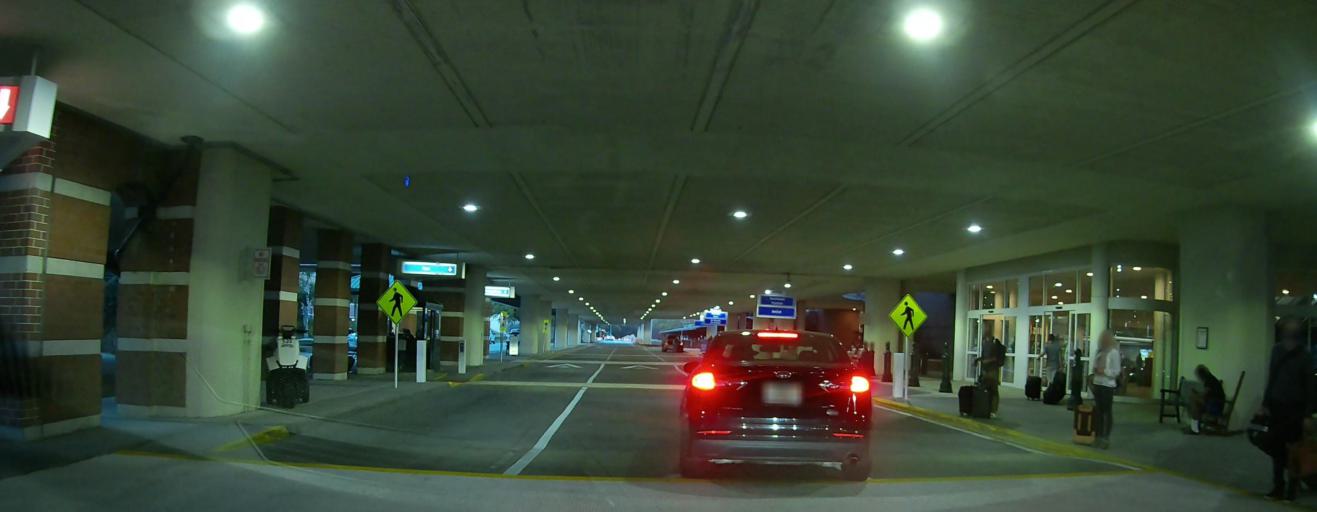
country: US
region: Georgia
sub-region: Chatham County
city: Pooler
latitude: 32.1358
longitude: -81.2103
